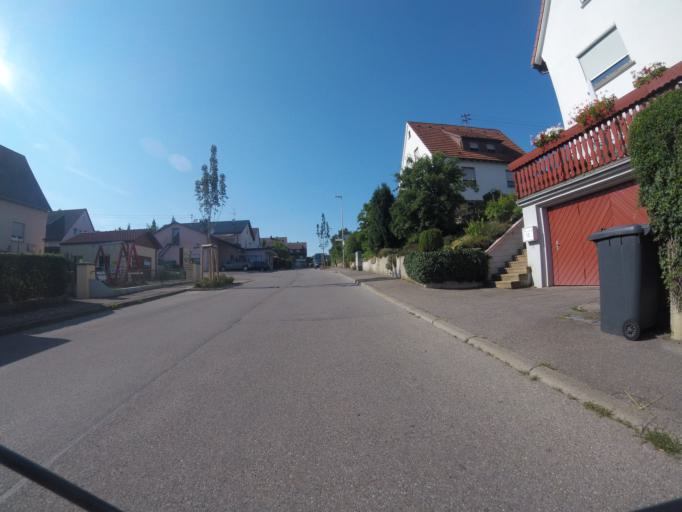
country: DE
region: Baden-Wuerttemberg
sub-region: Regierungsbezirk Stuttgart
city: Kirchberg an der Murr
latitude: 48.9624
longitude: 9.3292
